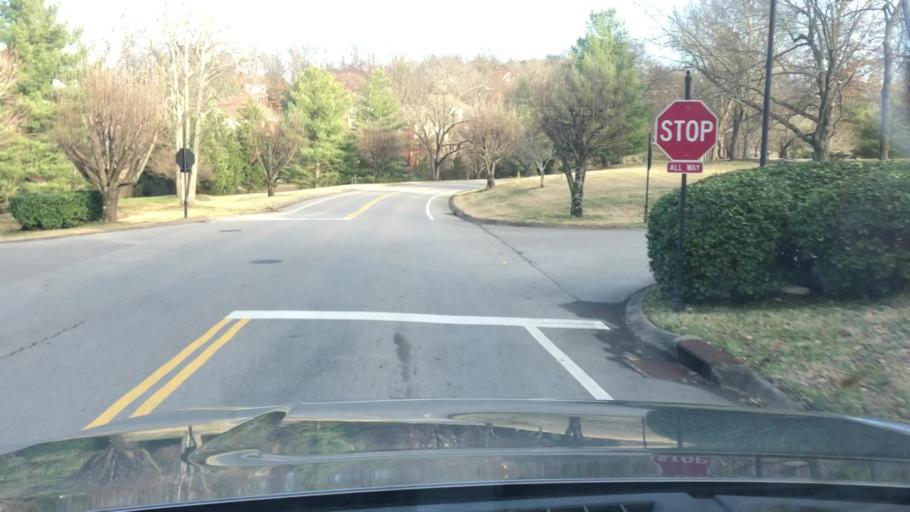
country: US
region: Tennessee
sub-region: Williamson County
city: Brentwood Estates
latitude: 35.9774
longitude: -86.7503
